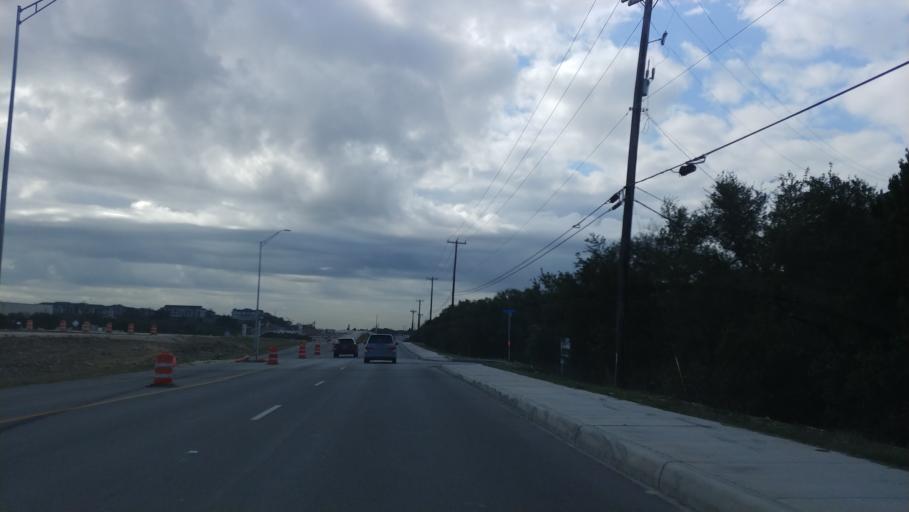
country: US
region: Texas
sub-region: Bexar County
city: Leon Valley
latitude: 29.4716
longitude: -98.7115
